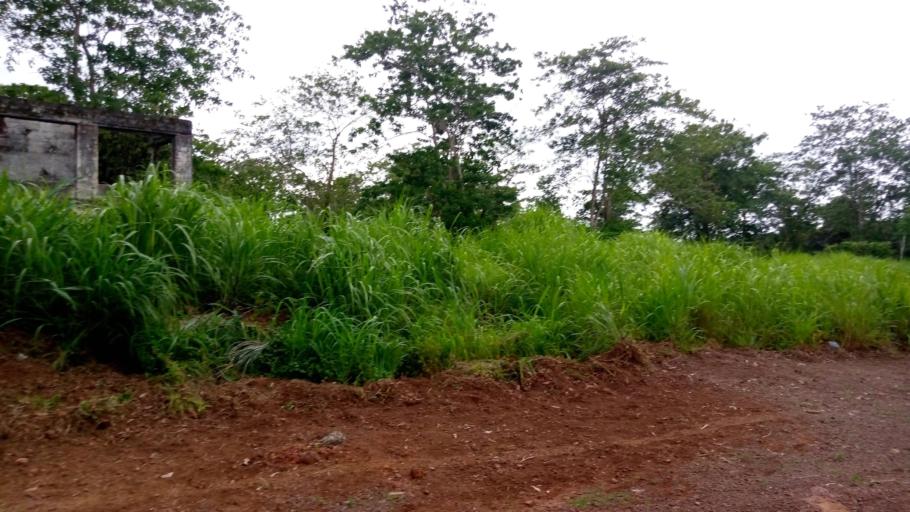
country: SL
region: Southern Province
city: Moyamba
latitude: 8.1604
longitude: -12.4449
